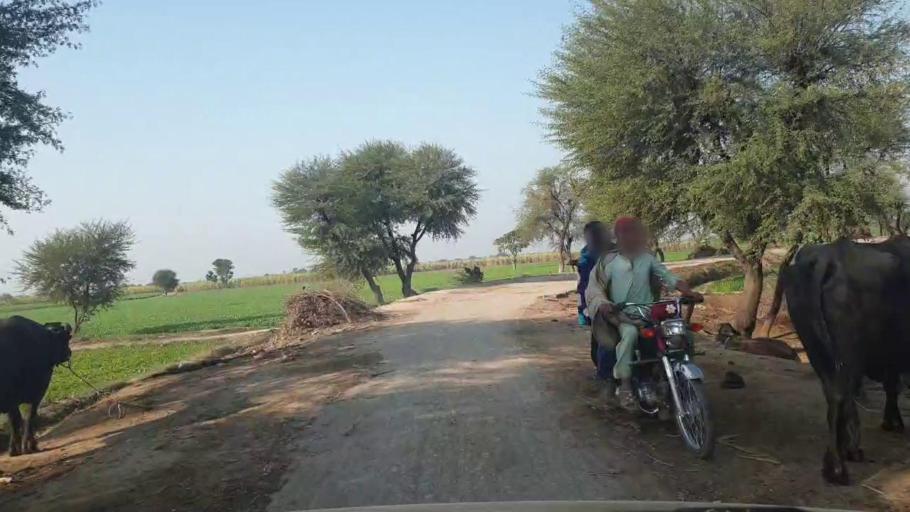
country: PK
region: Sindh
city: Tando Adam
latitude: 25.7368
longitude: 68.6130
